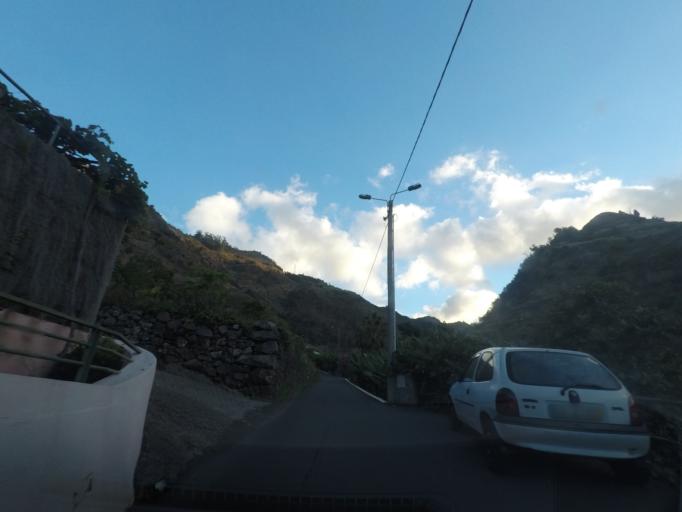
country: PT
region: Madeira
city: Ponta do Sol
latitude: 32.6871
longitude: -17.0752
